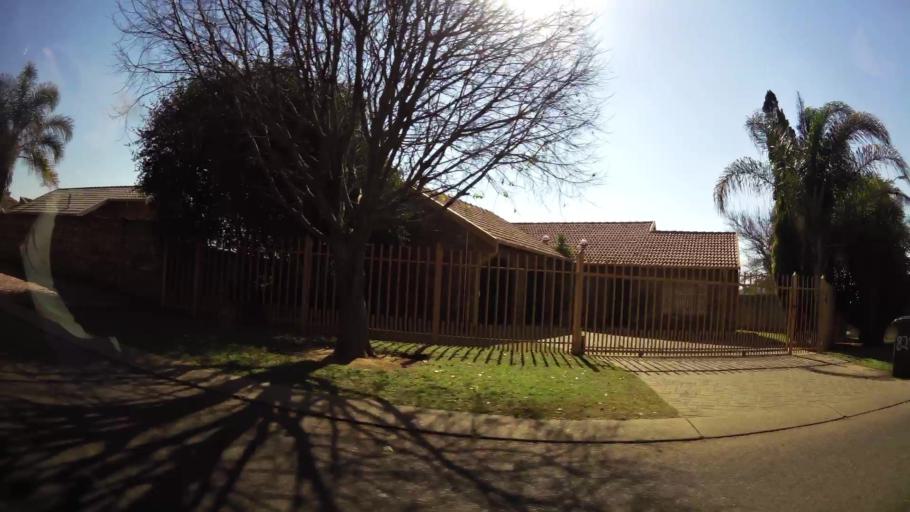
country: ZA
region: Gauteng
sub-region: City of Tshwane Metropolitan Municipality
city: Pretoria
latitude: -25.6513
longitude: 28.2525
